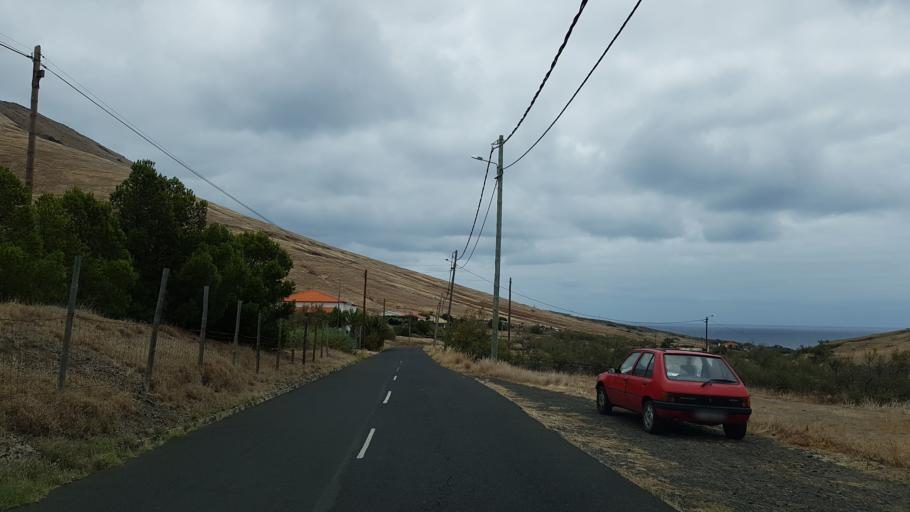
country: PT
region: Madeira
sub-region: Porto Santo
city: Vila de Porto Santo
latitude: 33.0722
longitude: -16.3074
